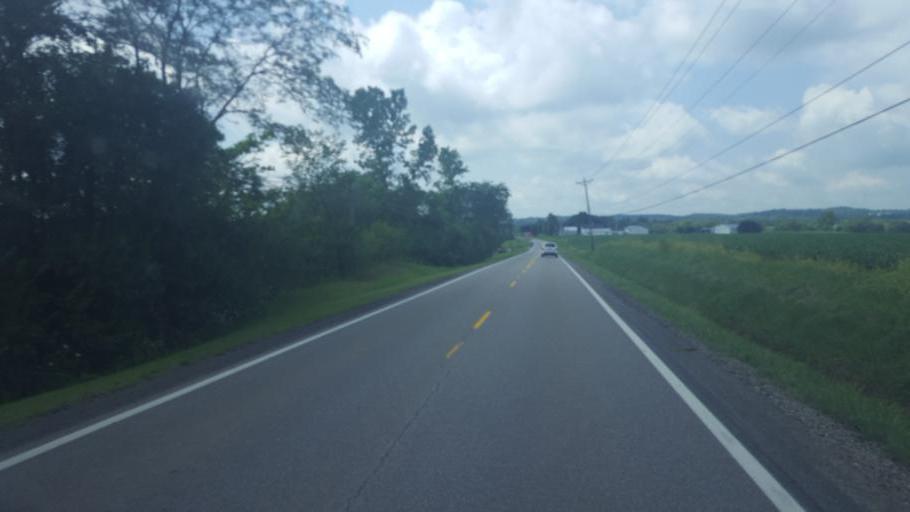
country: US
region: Ohio
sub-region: Fairfield County
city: Lancaster
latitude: 39.6367
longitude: -82.7345
